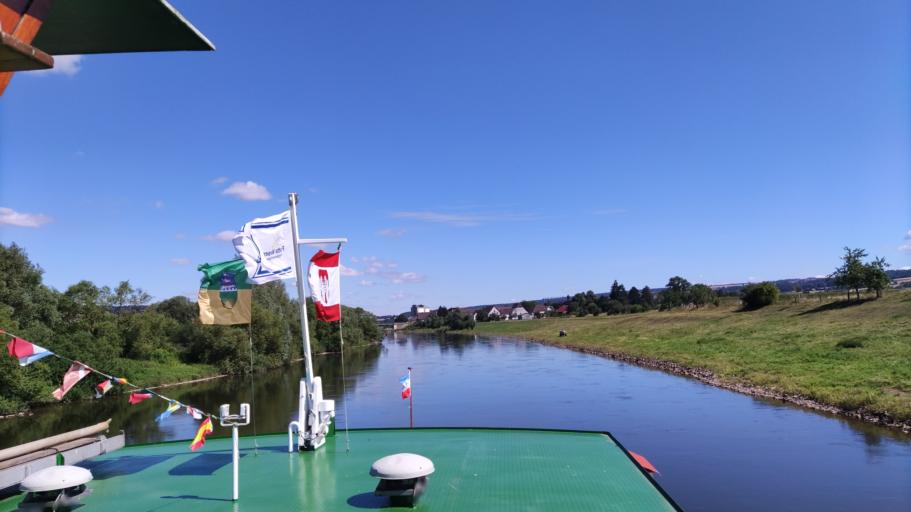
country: DE
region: North Rhine-Westphalia
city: Beverungen
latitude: 51.6555
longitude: 9.3774
